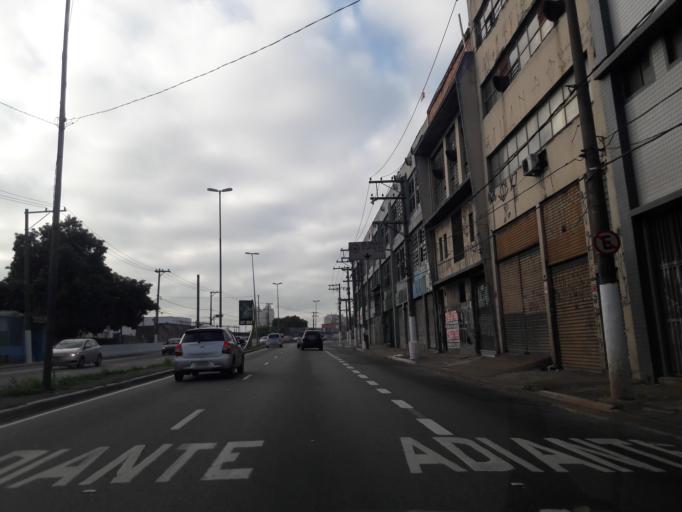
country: BR
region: Sao Paulo
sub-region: Sao Caetano Do Sul
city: Sao Caetano do Sul
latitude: -23.6056
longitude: -46.5996
